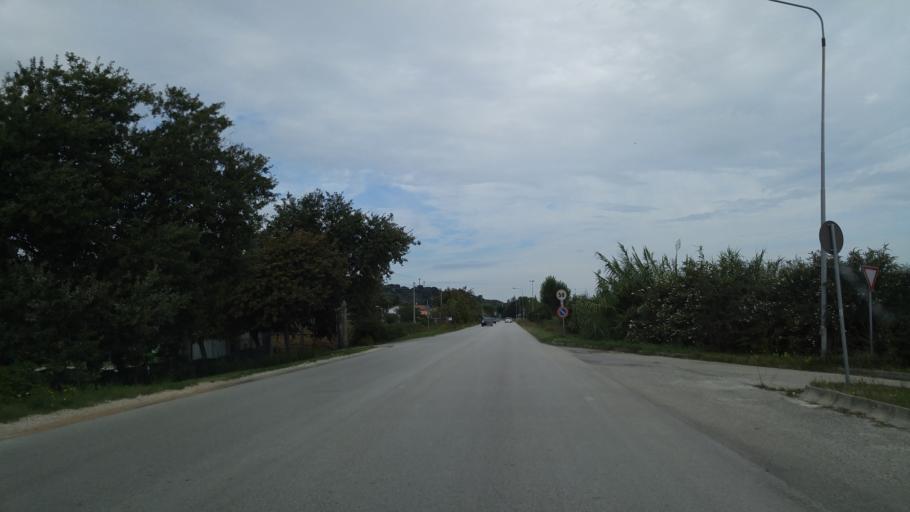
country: IT
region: The Marches
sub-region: Provincia di Pesaro e Urbino
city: Rosciano
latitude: 43.8134
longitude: 13.0019
